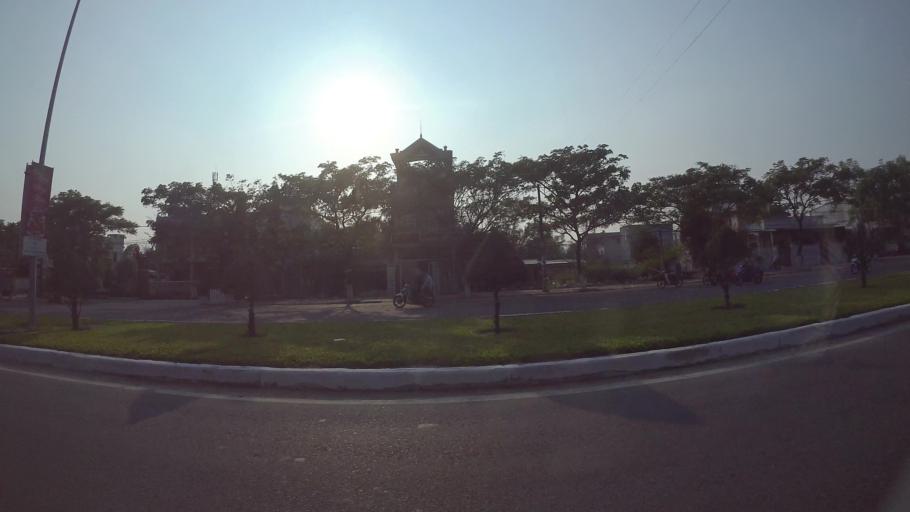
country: VN
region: Da Nang
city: Ngu Hanh Son
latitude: 15.9665
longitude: 108.2548
